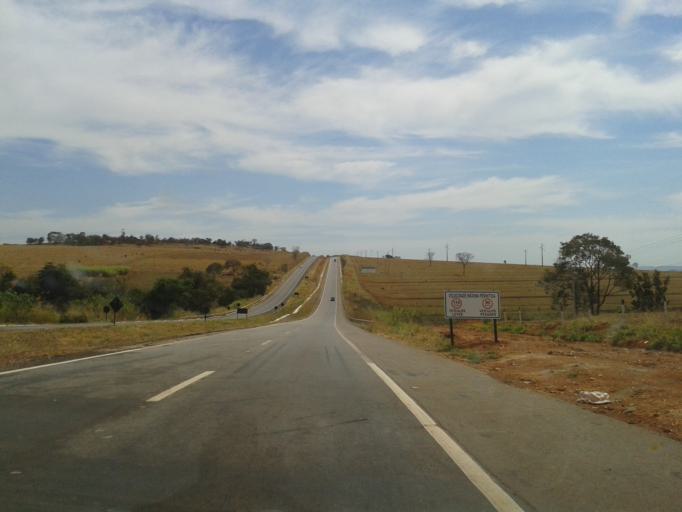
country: BR
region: Goias
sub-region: Itaberai
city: Itaberai
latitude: -16.1258
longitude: -49.6516
